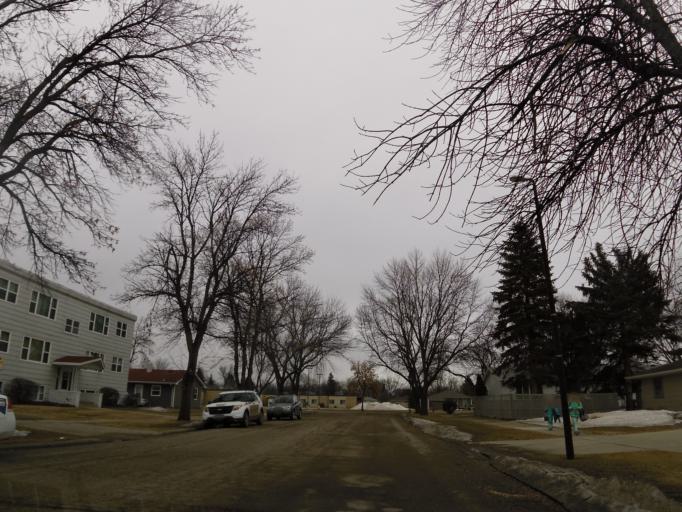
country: US
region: North Dakota
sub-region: Walsh County
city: Grafton
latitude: 48.4110
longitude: -97.4199
